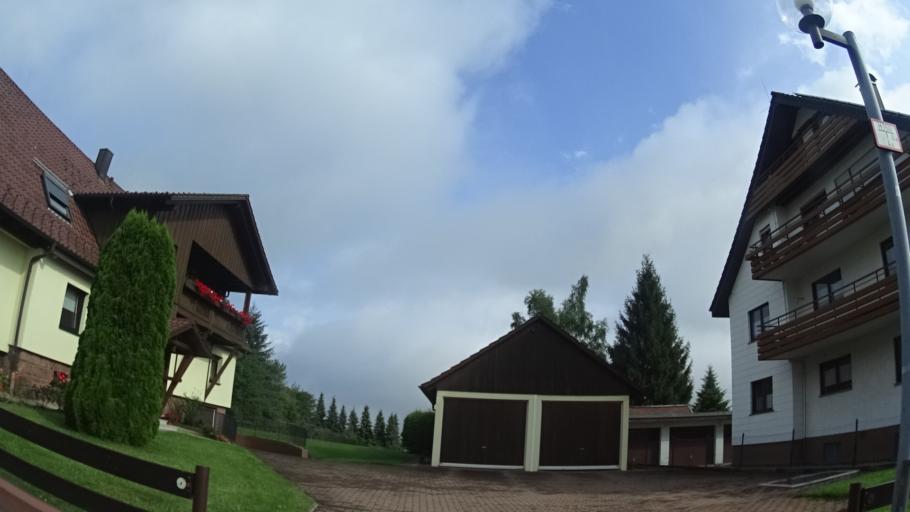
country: DE
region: Baden-Wuerttemberg
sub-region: Karlsruhe Region
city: Dobel
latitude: 48.7944
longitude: 8.4928
